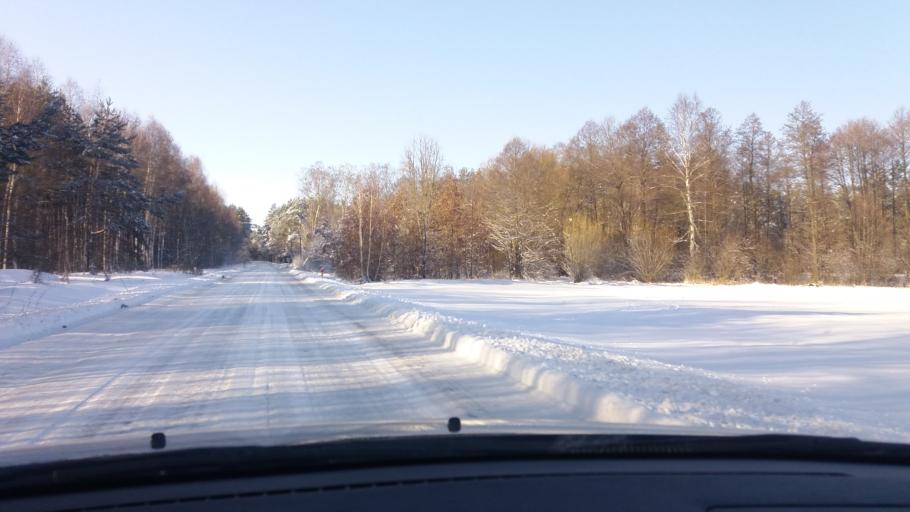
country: PL
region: Masovian Voivodeship
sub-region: Powiat mlawski
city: Dzierzgowo
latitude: 53.3316
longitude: 20.6475
